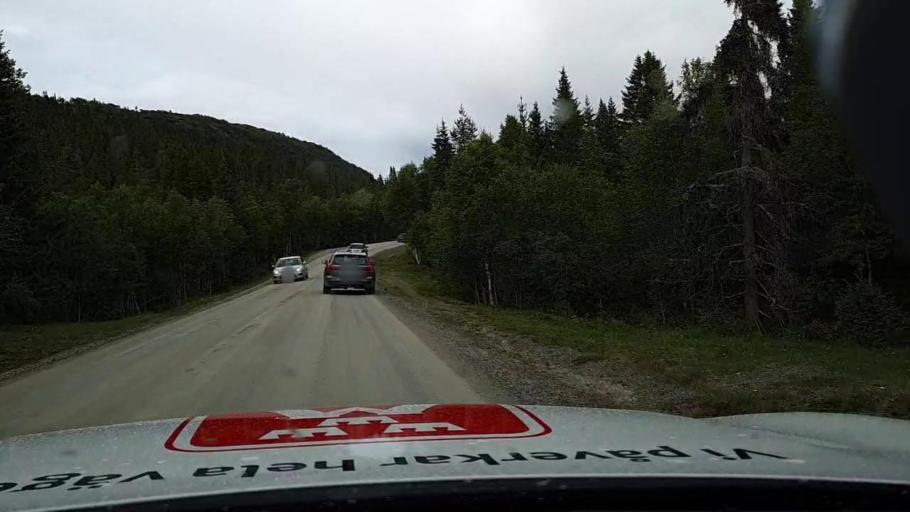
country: SE
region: Jaemtland
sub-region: Are Kommun
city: Are
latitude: 62.5842
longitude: 12.5961
